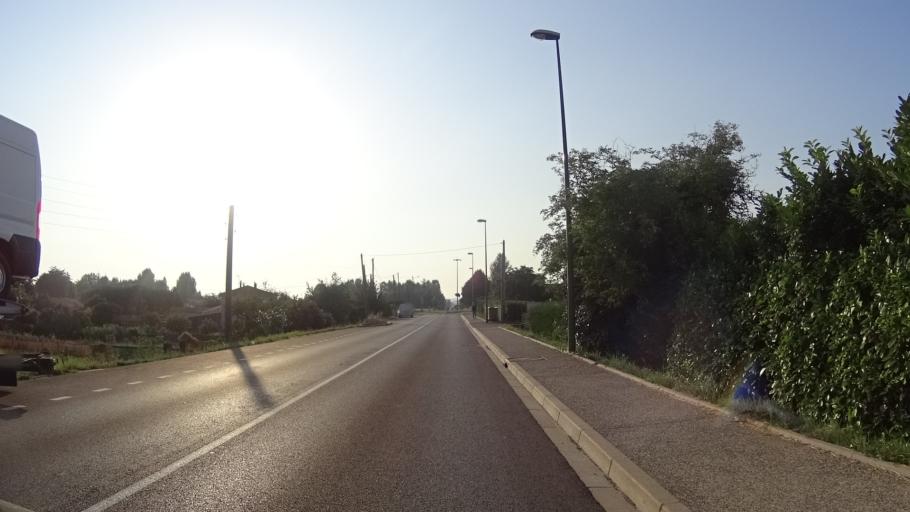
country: FR
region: Midi-Pyrenees
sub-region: Departement de l'Ariege
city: Mirepoix
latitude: 43.0878
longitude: 1.8802
